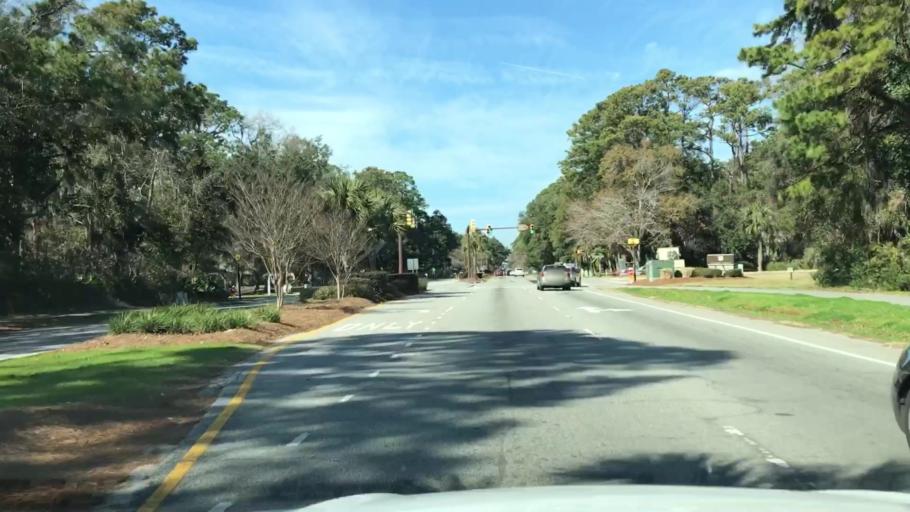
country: US
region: South Carolina
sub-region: Beaufort County
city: Hilton Head Island
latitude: 32.1473
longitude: -80.7557
